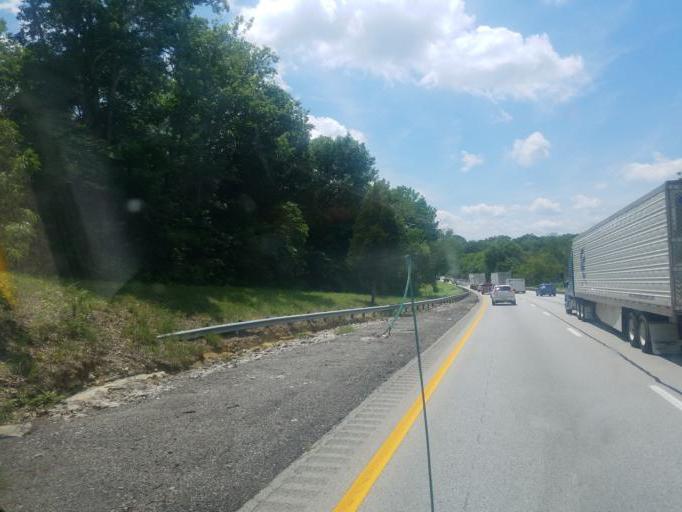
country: US
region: Kentucky
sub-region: Oldham County
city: Orchard Grass Hills
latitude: 38.3384
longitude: -85.5221
